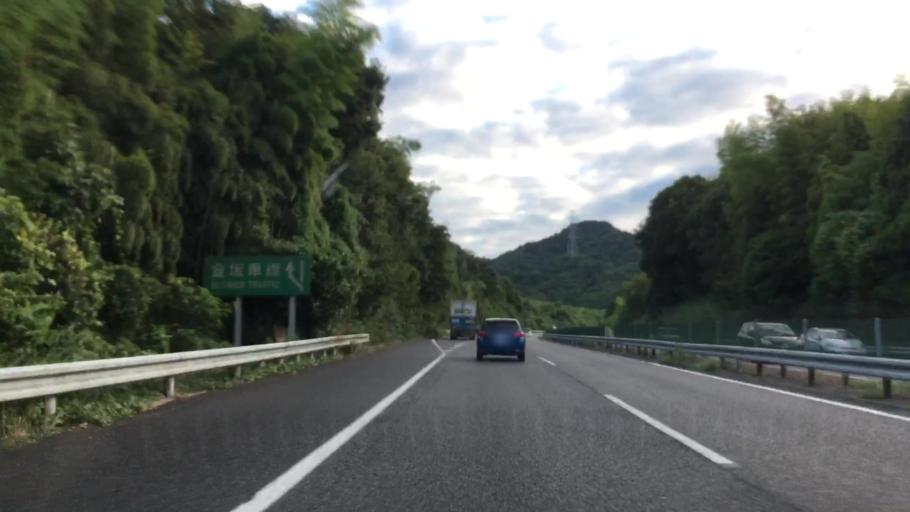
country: JP
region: Yamaguchi
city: Shimonoseki
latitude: 34.0424
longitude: 130.9862
